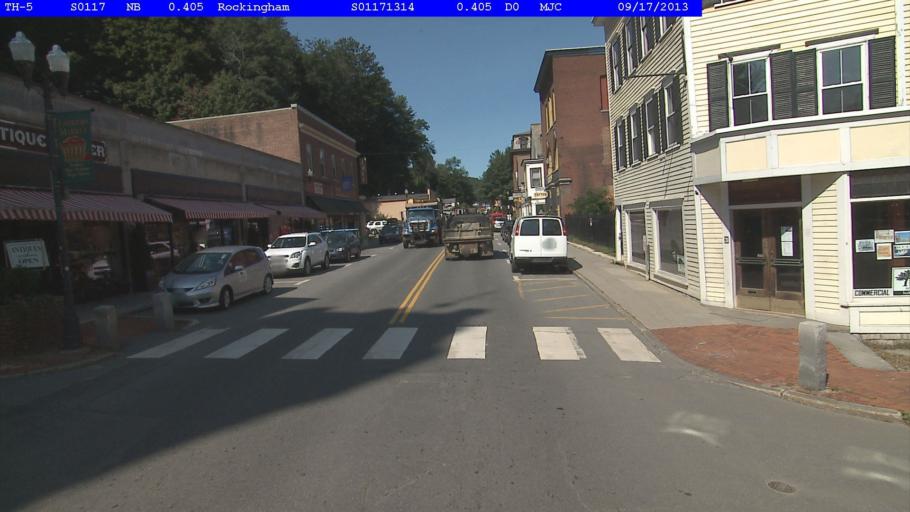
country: US
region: Vermont
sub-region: Windham County
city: Bellows Falls
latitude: 43.1343
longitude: -72.4446
